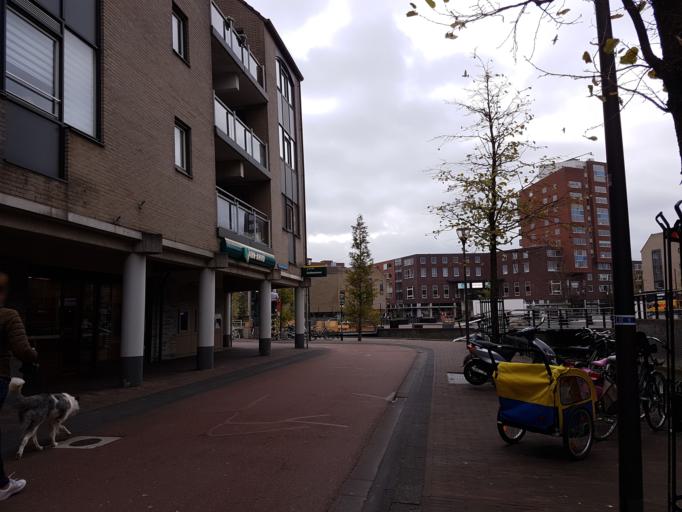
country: NL
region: Utrecht
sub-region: Gemeente Houten
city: Houten
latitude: 52.0358
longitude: 5.1706
